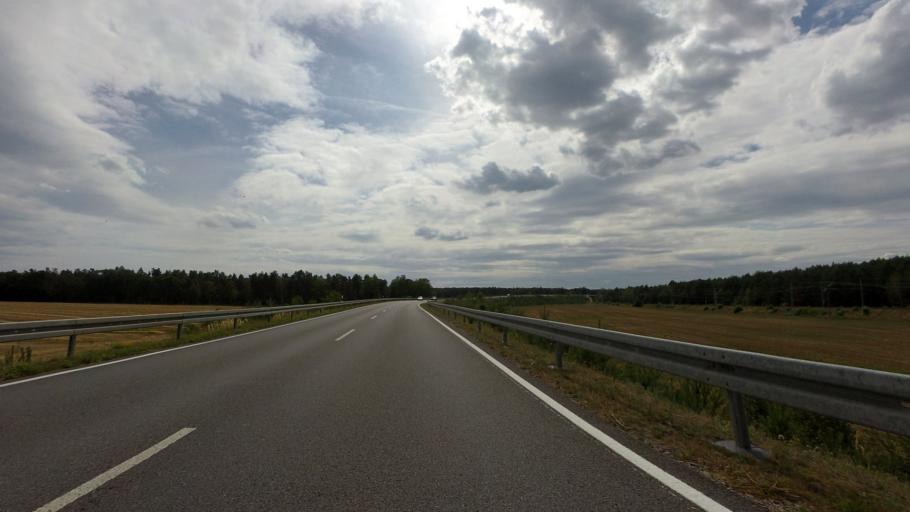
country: DE
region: Brandenburg
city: Spremberg
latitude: 51.5871
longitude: 14.3509
